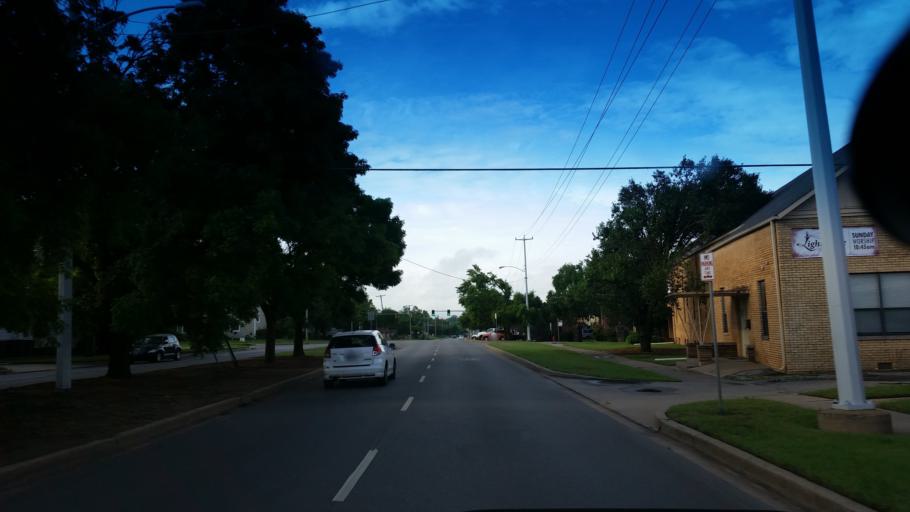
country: US
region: Oklahoma
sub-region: Oklahoma County
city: Edmond
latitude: 35.6516
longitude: -97.4783
